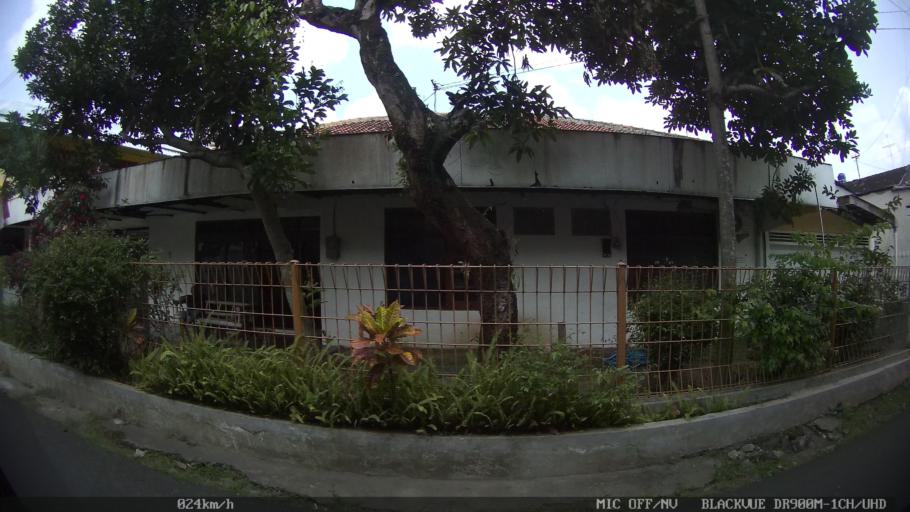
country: ID
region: Daerah Istimewa Yogyakarta
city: Yogyakarta
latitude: -7.7855
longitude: 110.3826
